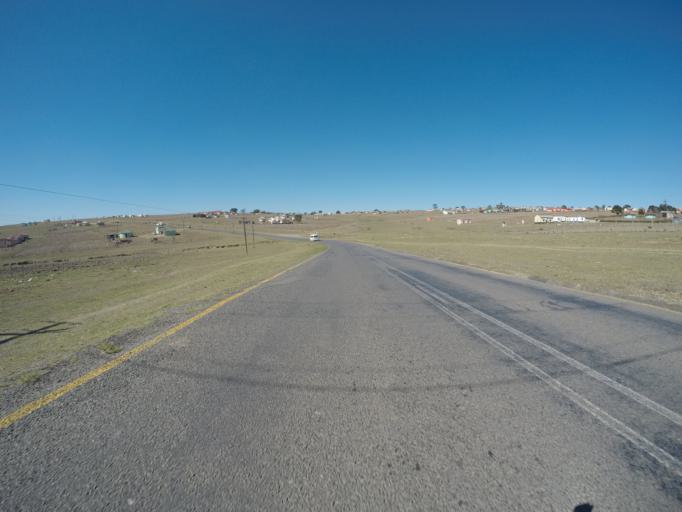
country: ZA
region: Eastern Cape
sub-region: OR Tambo District Municipality
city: Mthatha
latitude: -31.8806
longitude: 28.7558
